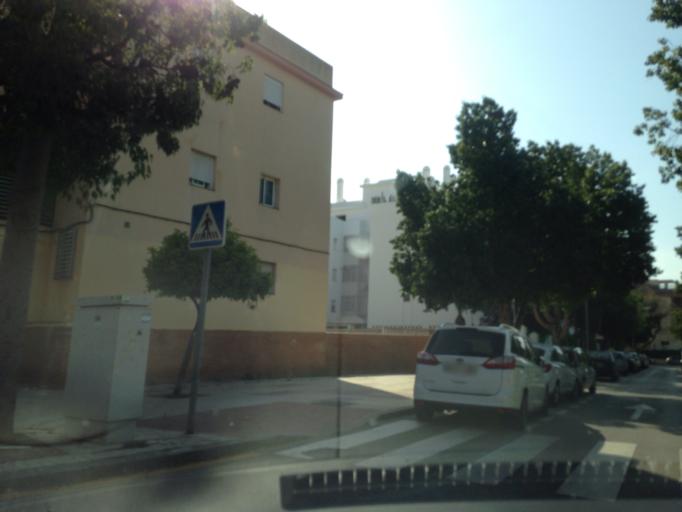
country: ES
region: Andalusia
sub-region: Provincia de Malaga
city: Malaga
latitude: 36.7223
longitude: -4.4841
